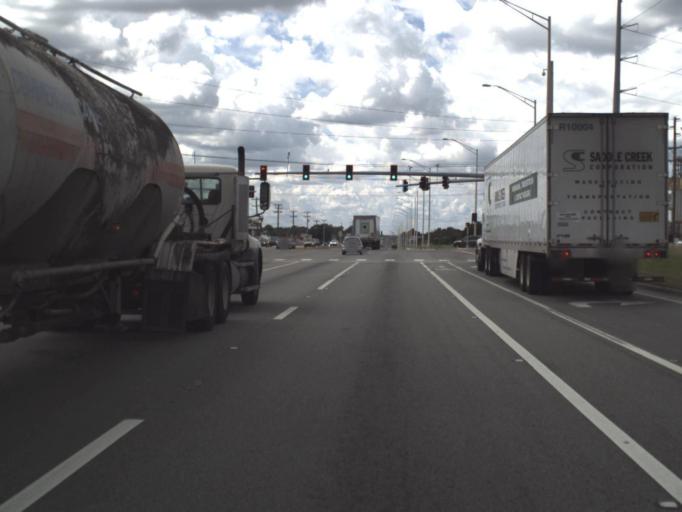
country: US
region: Florida
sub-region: Polk County
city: Crystal Lake
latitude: 28.0077
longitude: -81.9071
